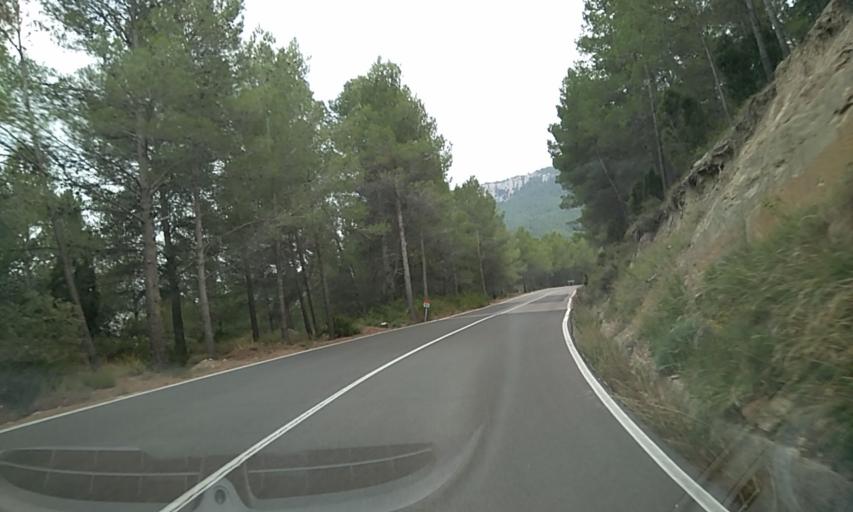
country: ES
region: Valencia
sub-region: Provincia de Castello
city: Puebla de Arenoso
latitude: 40.0946
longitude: -0.5678
